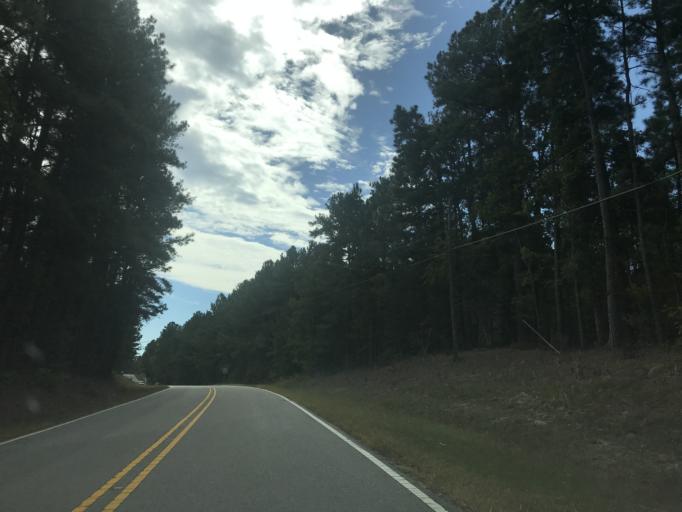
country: US
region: North Carolina
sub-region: Wake County
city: Rolesville
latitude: 35.8742
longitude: -78.4771
